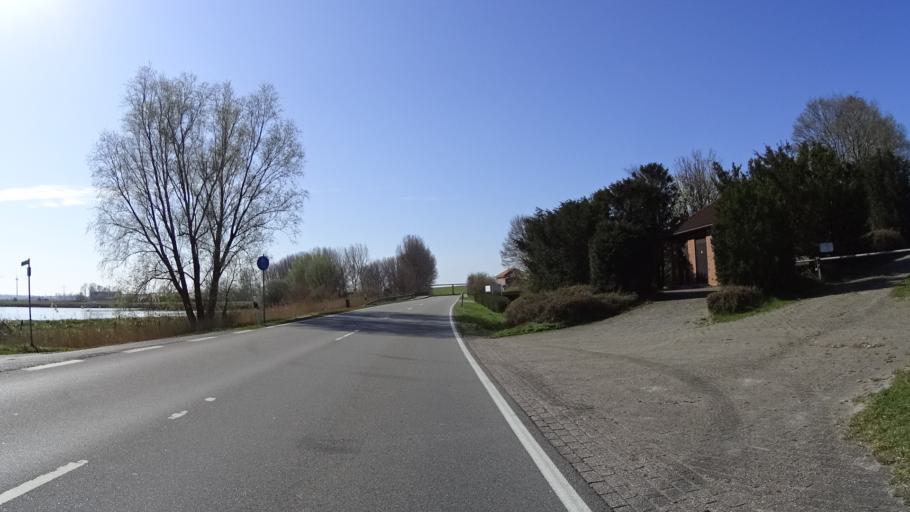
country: DE
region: Lower Saxony
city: Jemgum
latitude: 53.2862
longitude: 7.4049
